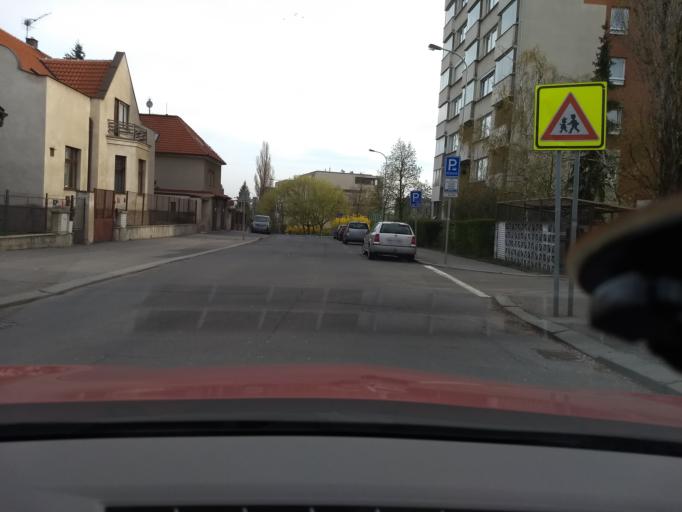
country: CZ
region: Central Bohemia
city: Horomerice
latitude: 50.0973
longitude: 14.3474
